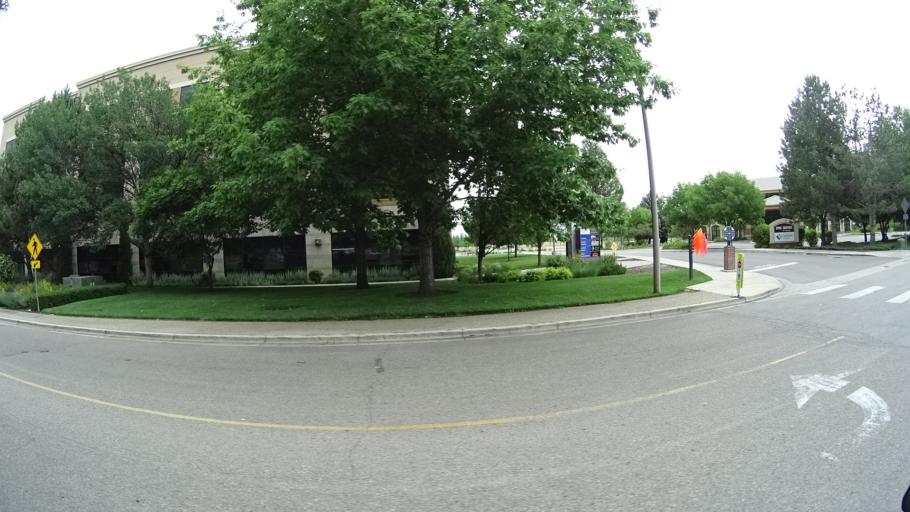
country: US
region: Idaho
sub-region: Ada County
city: Meridian
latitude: 43.6011
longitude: -116.3523
